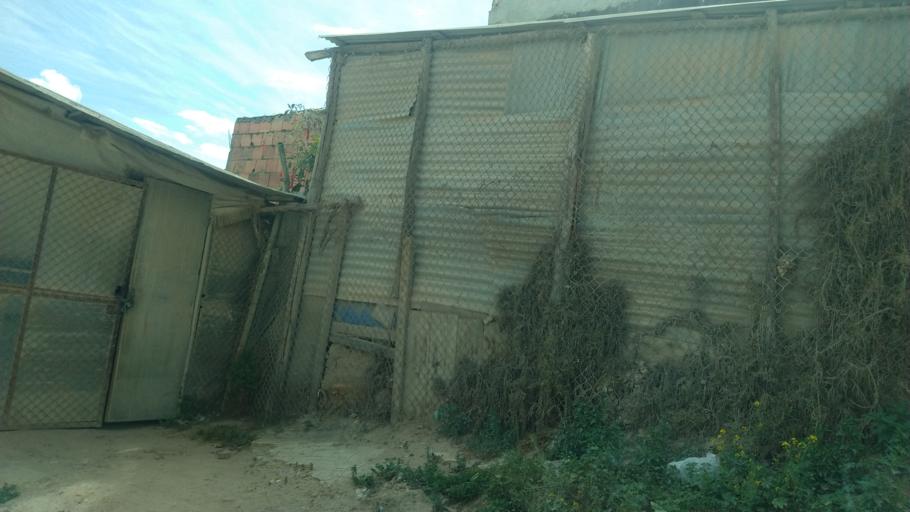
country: CO
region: Cundinamarca
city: Soacha
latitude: 4.5659
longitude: -74.1819
